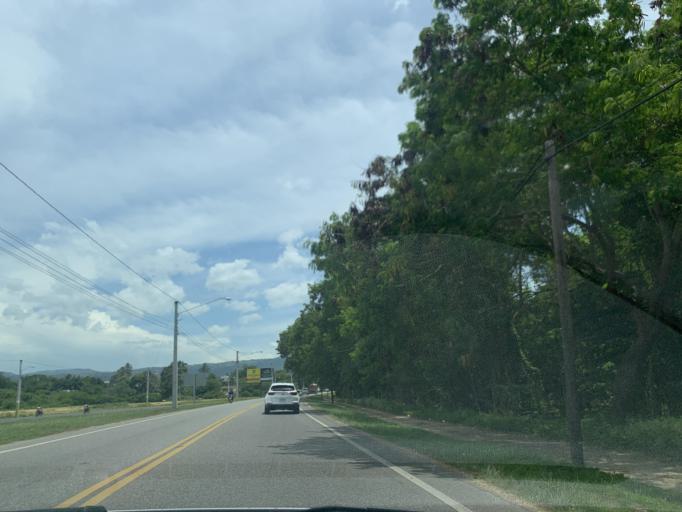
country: DO
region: Puerto Plata
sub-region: Puerto Plata
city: Puerto Plata
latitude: 19.7244
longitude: -70.6097
